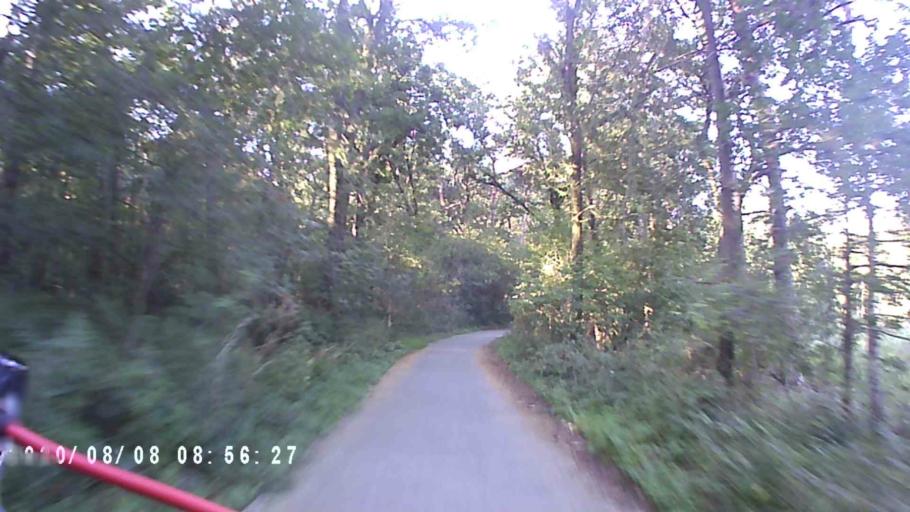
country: NL
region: Groningen
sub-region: Gemeente Leek
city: Leek
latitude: 53.0550
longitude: 6.3245
